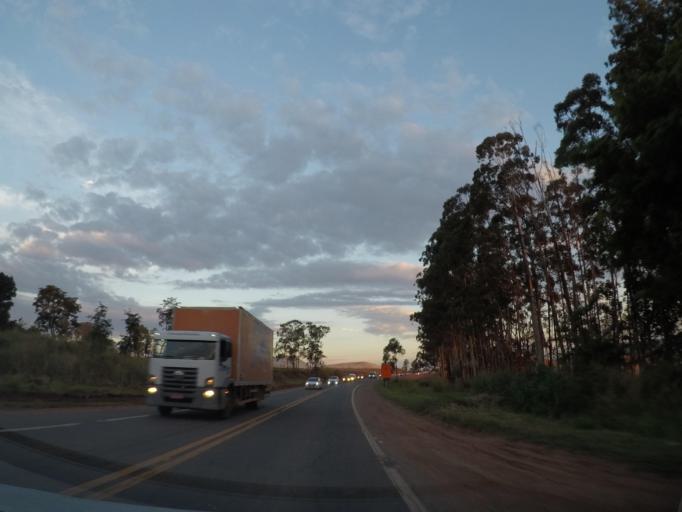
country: BR
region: Sao Paulo
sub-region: Itupeva
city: Itupeva
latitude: -23.0441
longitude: -47.1024
